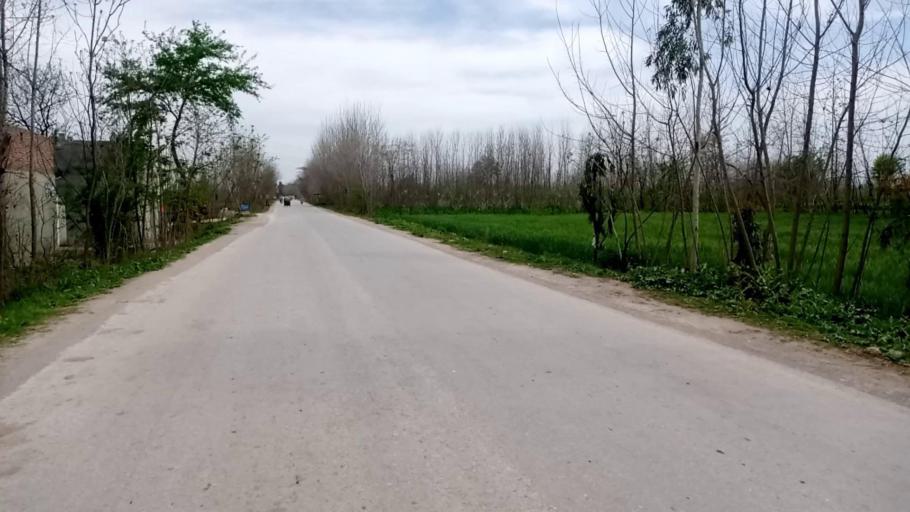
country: PK
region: Khyber Pakhtunkhwa
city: Charsadda
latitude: 34.0631
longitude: 71.6923
